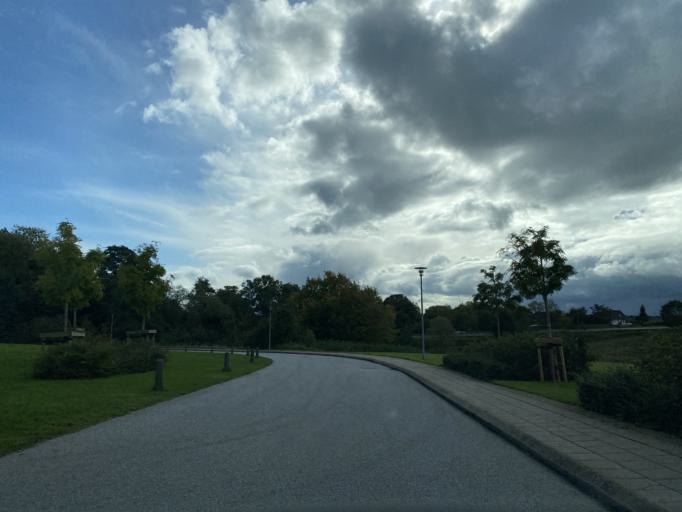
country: DK
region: South Denmark
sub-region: Haderslev Kommune
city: Haderslev
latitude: 55.2459
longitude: 9.4453
